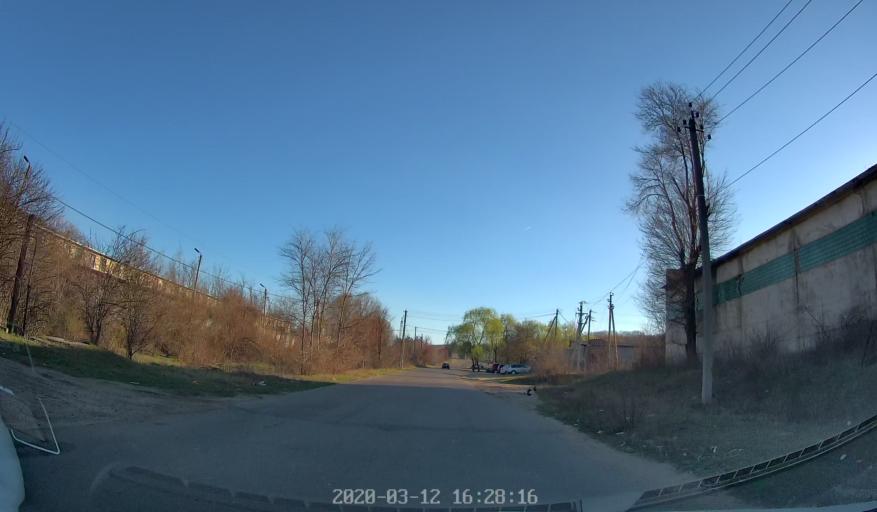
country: MD
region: Anenii Noi
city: Anenii Noi
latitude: 46.8693
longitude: 29.2256
